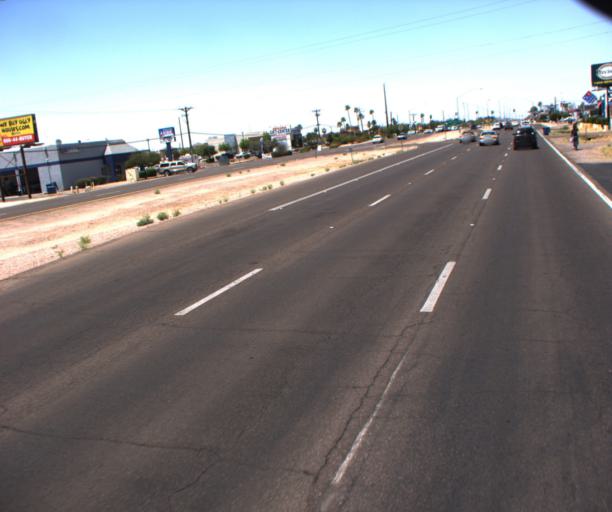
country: US
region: Arizona
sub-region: Pinal County
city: Apache Junction
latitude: 33.4154
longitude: -111.5952
